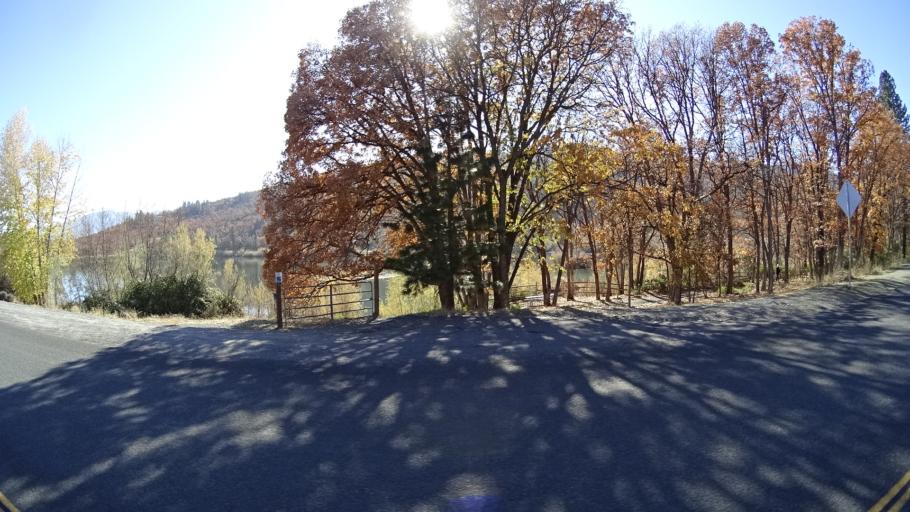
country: US
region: California
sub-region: Siskiyou County
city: Yreka
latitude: 41.7132
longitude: -122.6530
